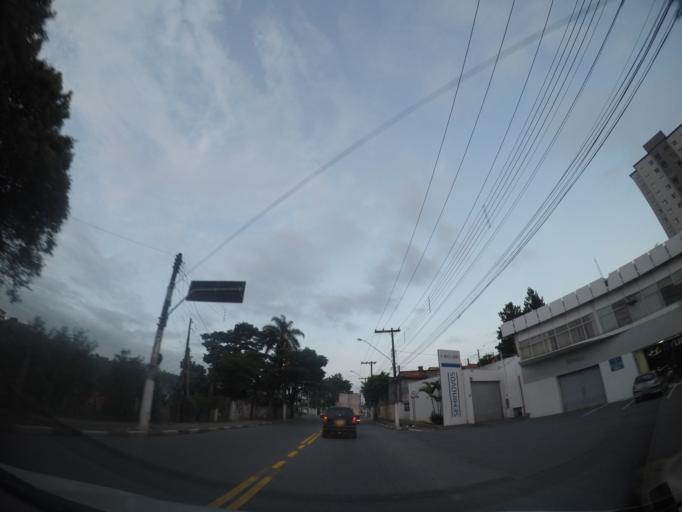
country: BR
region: Sao Paulo
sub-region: Aruja
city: Aruja
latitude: -23.3895
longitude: -46.3155
